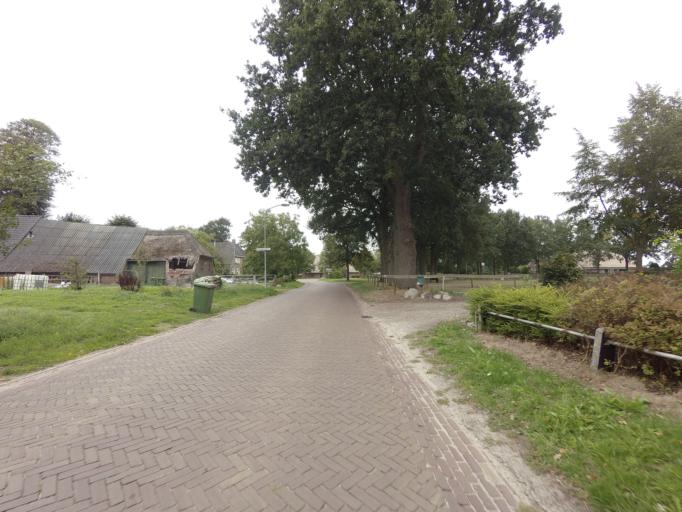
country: NL
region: Drenthe
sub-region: Gemeente Assen
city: Assen
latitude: 52.9955
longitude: 6.6324
